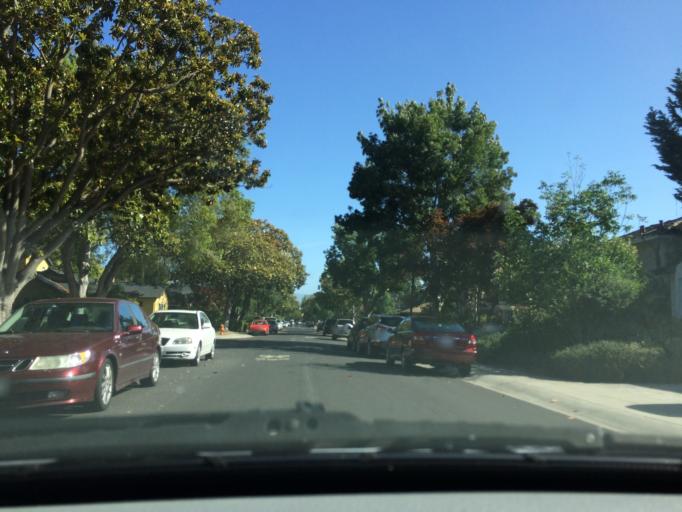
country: US
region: California
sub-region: Santa Clara County
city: Palo Alto
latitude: 37.4484
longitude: -122.1335
